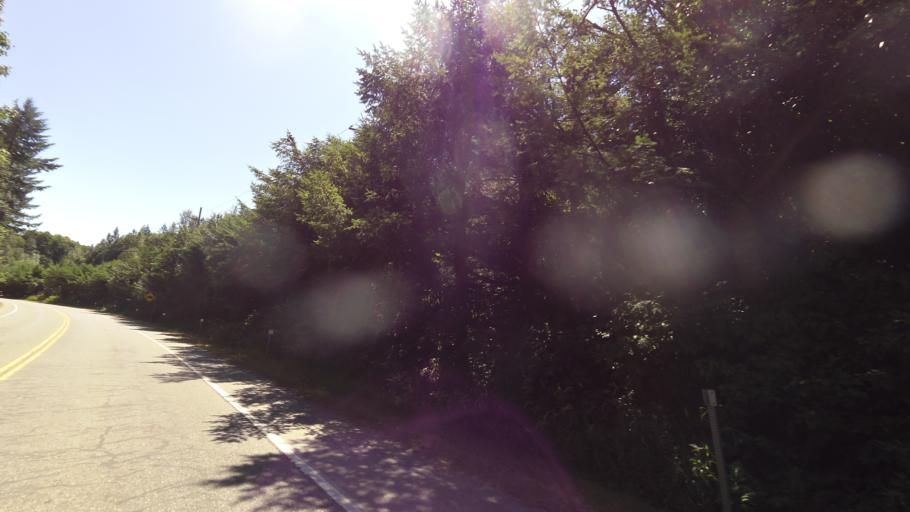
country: CA
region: British Columbia
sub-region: Fraser Valley Regional District
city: Chilliwack
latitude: 49.2269
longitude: -122.0161
